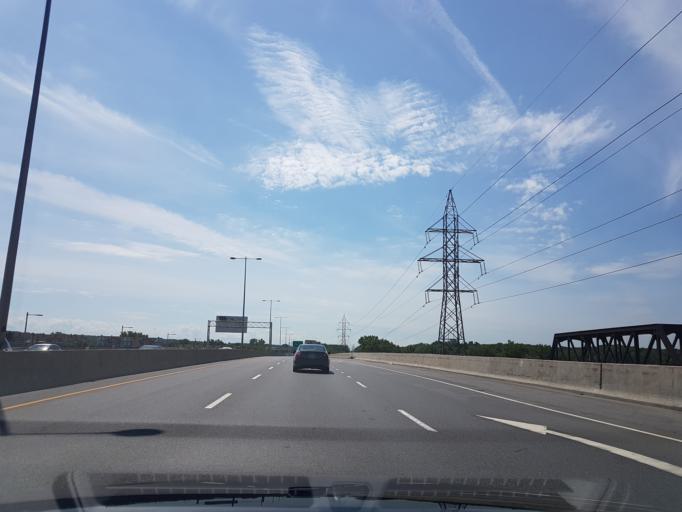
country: CA
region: Quebec
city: Sainte-Anne-de-Bellevue
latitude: 45.4044
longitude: -73.9549
